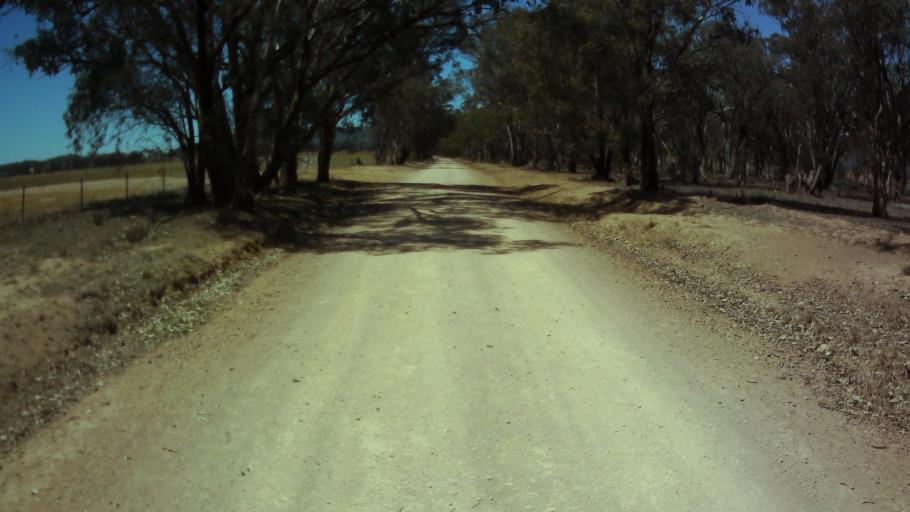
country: AU
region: New South Wales
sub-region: Weddin
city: Grenfell
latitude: -33.9216
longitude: 148.0787
